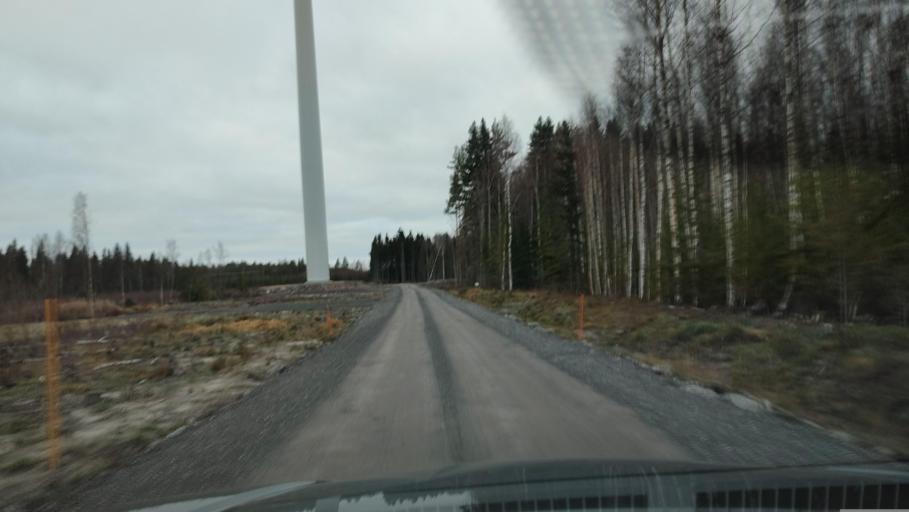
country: FI
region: Southern Ostrobothnia
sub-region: Suupohja
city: Karijoki
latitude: 62.2192
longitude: 21.5999
